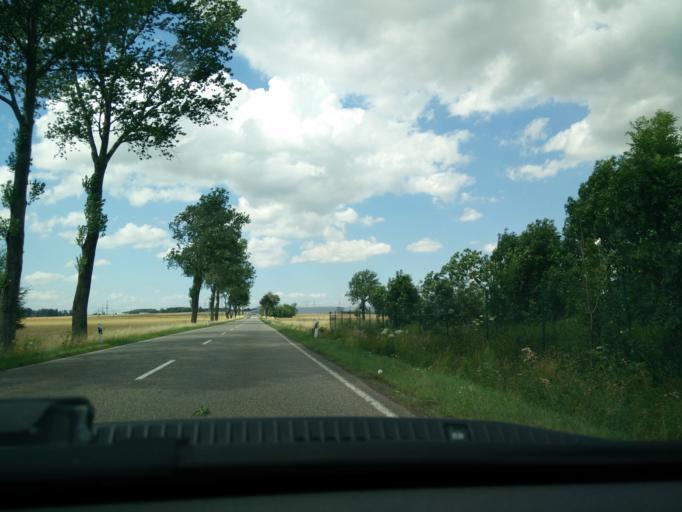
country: DE
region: Saxony
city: Wittgensdorf
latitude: 50.8666
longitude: 12.8472
